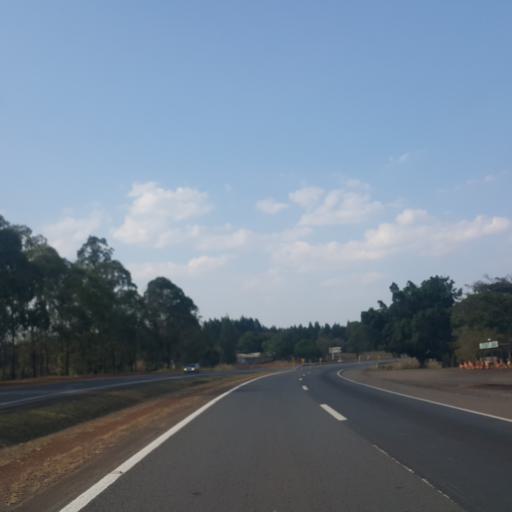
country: BR
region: Goias
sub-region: Abadiania
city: Abadiania
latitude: -16.1857
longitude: -48.6974
